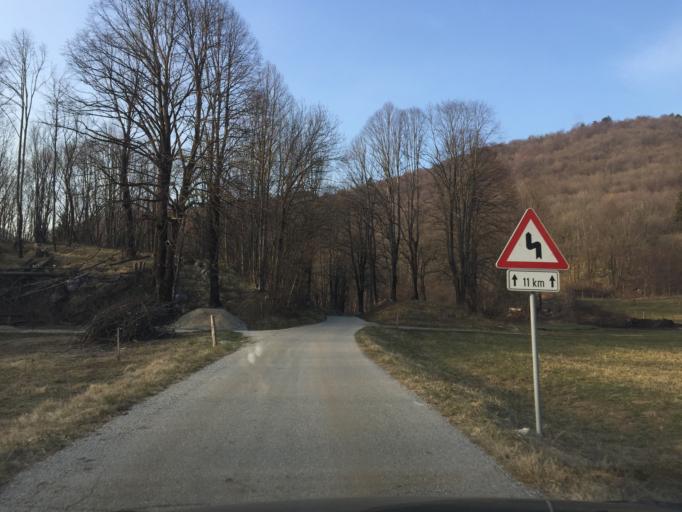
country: SI
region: Kanal
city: Kanal
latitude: 46.0499
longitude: 13.6736
